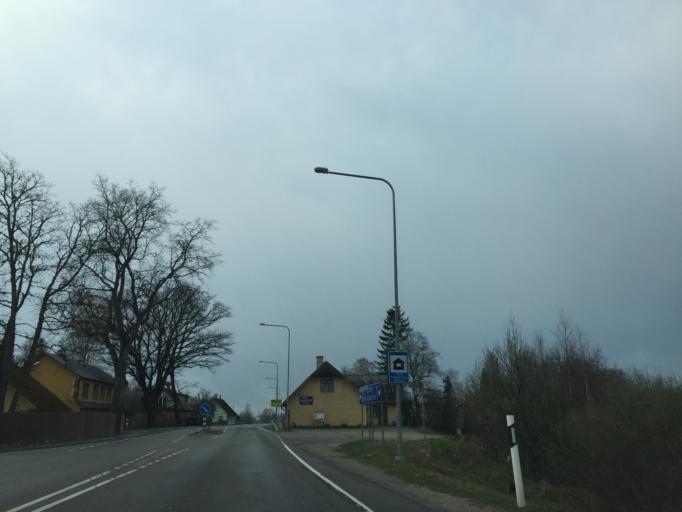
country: EE
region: Tartu
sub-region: UElenurme vald
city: Ulenurme
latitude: 58.1448
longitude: 26.7027
